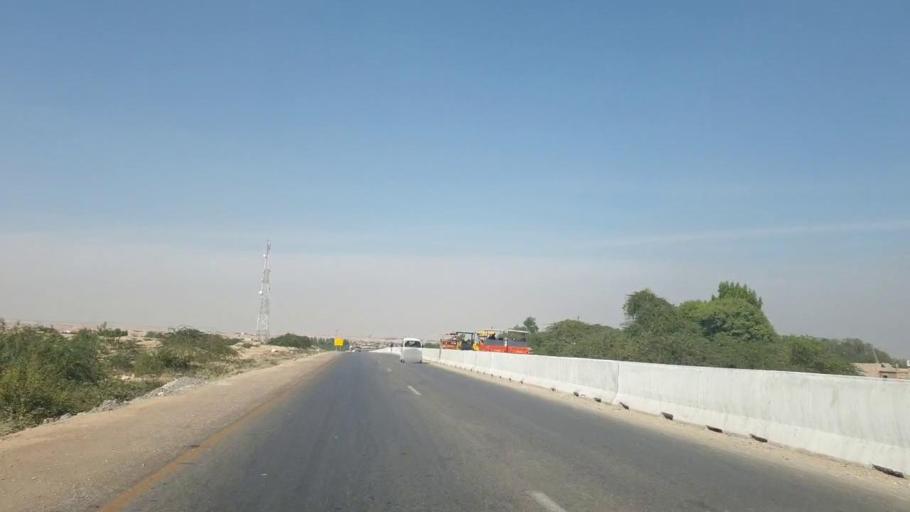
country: PK
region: Sindh
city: Hala
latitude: 25.7155
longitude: 68.2951
